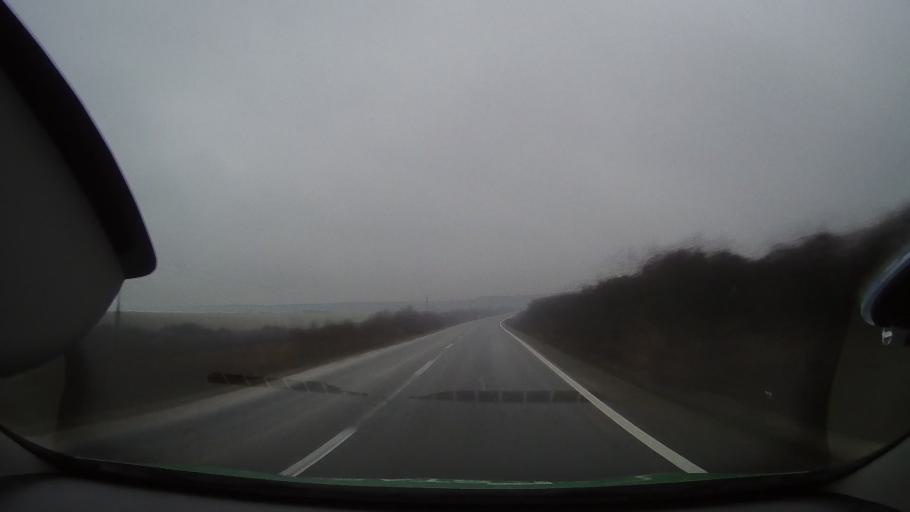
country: RO
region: Bihor
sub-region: Comuna Olcea
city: Olcea
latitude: 46.7104
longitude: 21.9593
